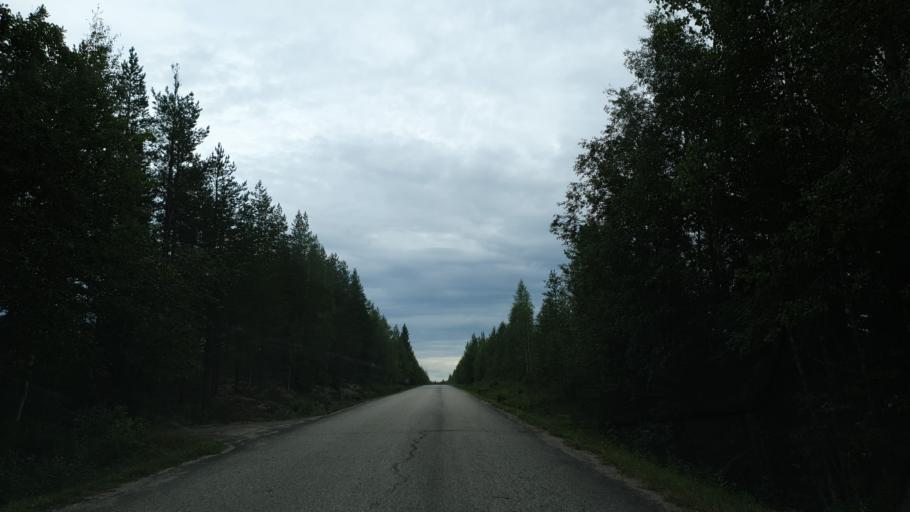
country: FI
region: Kainuu
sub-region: Kehys-Kainuu
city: Kuhmo
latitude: 64.3512
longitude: 29.1183
